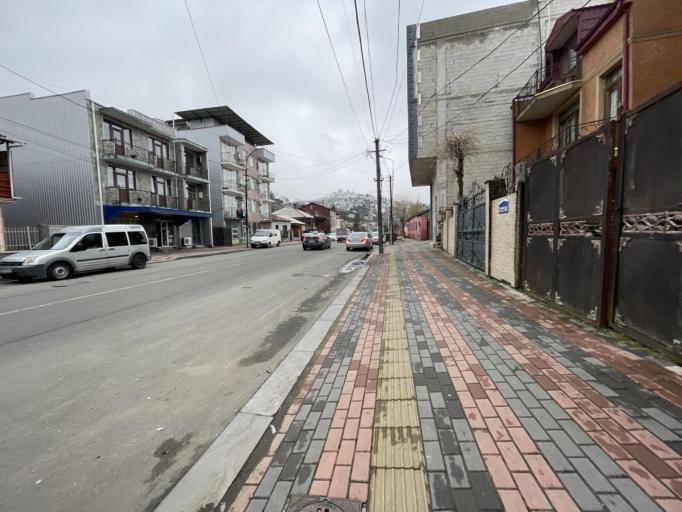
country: GE
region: Ajaria
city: Batumi
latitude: 41.6369
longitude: 41.6421
